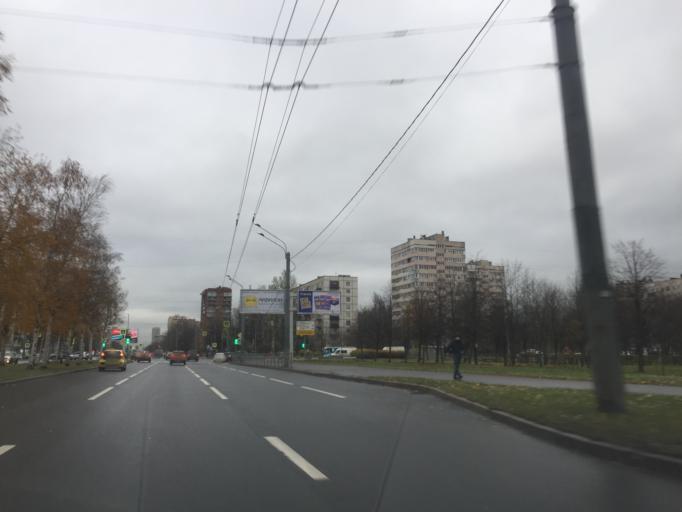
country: RU
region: St.-Petersburg
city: Grazhdanka
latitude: 60.0299
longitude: 30.3909
